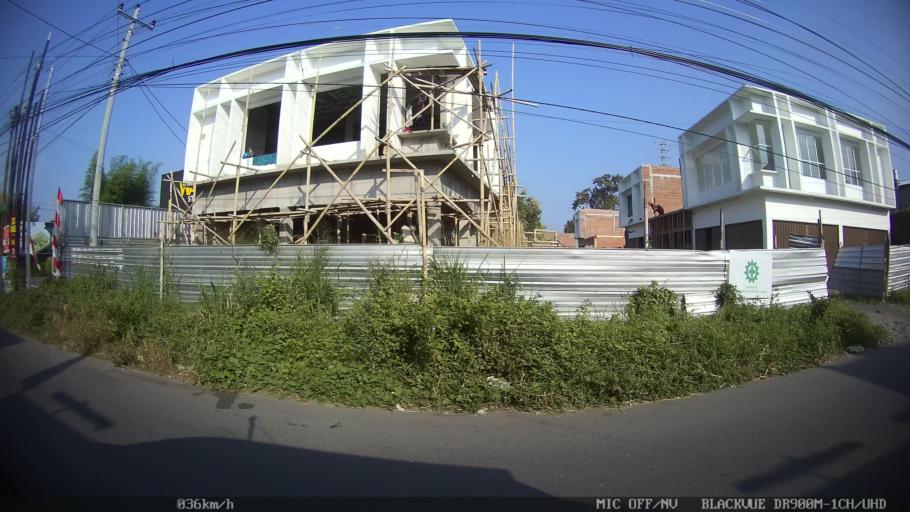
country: ID
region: Daerah Istimewa Yogyakarta
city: Depok
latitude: -7.7732
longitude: 110.4048
